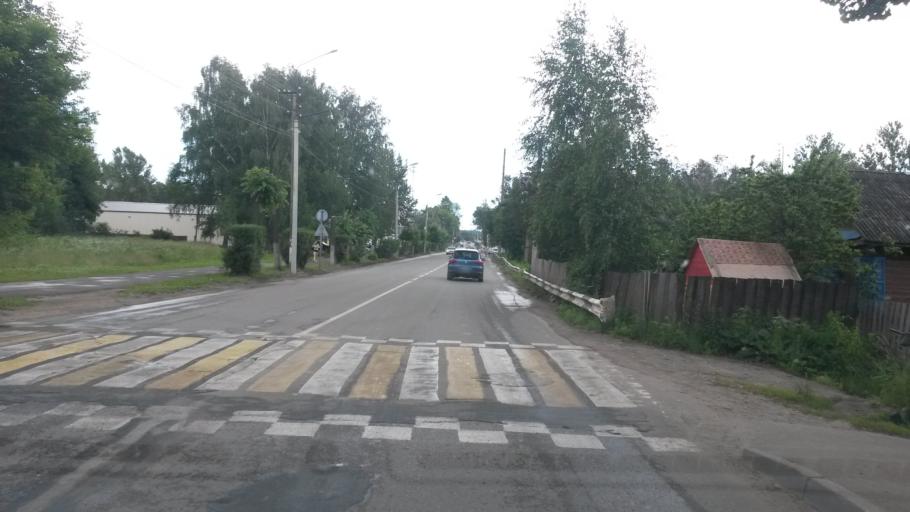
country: RU
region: Jaroslavl
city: Gavrilov-Yam
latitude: 57.3071
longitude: 39.8523
